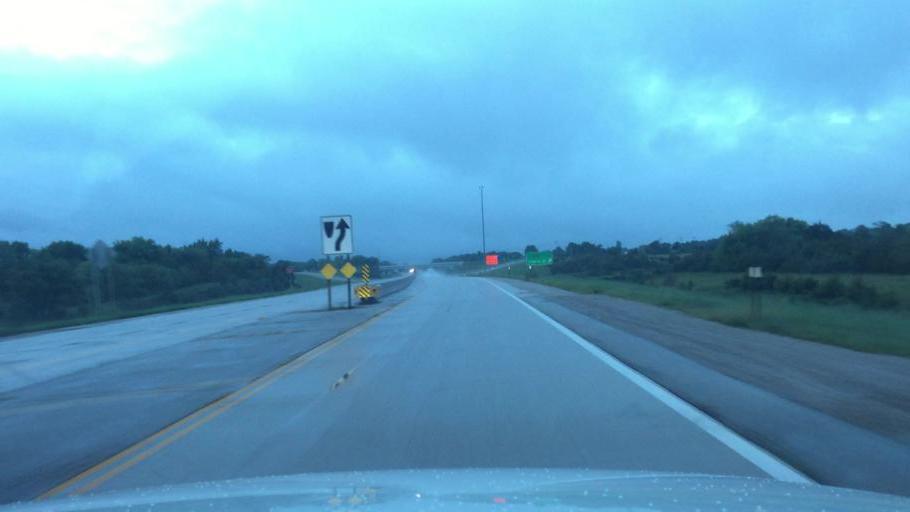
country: US
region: Kansas
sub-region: Neosho County
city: Chanute
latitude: 37.6948
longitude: -95.4795
